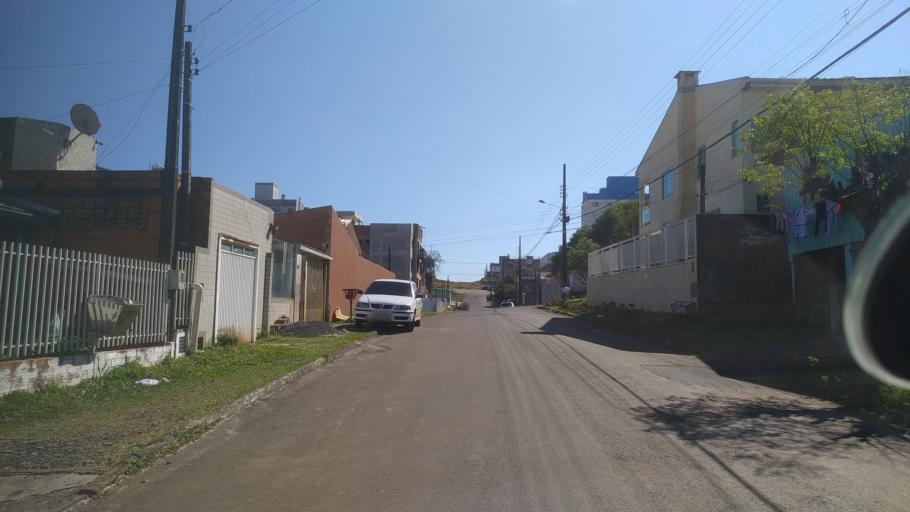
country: BR
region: Santa Catarina
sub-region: Chapeco
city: Chapeco
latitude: -27.0912
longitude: -52.5901
